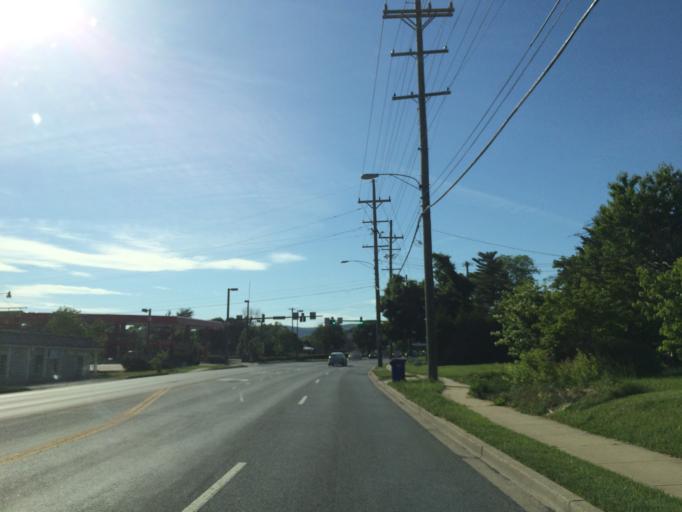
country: US
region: Maryland
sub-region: Frederick County
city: Frederick
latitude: 39.4261
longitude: -77.4296
